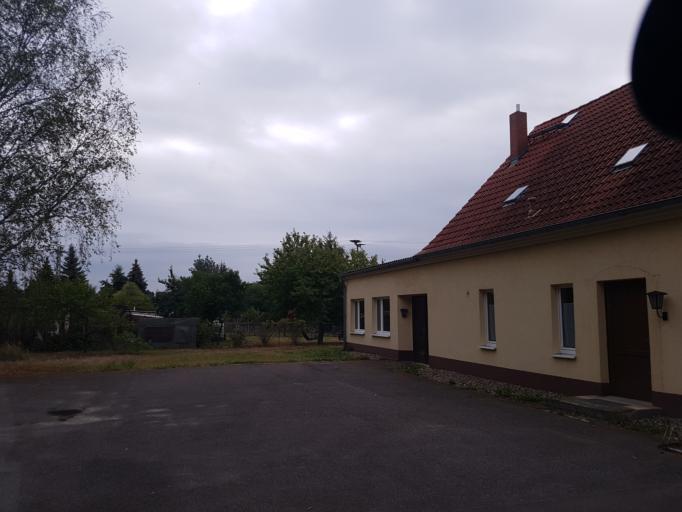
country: DE
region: Brandenburg
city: Calau
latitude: 51.7719
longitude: 13.8747
